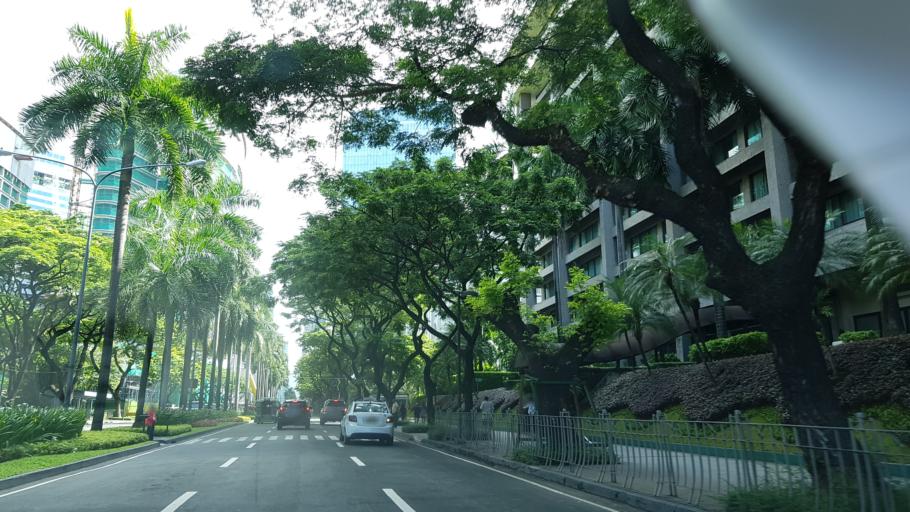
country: PH
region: Metro Manila
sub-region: Makati City
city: Makati City
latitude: 14.5551
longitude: 121.0250
